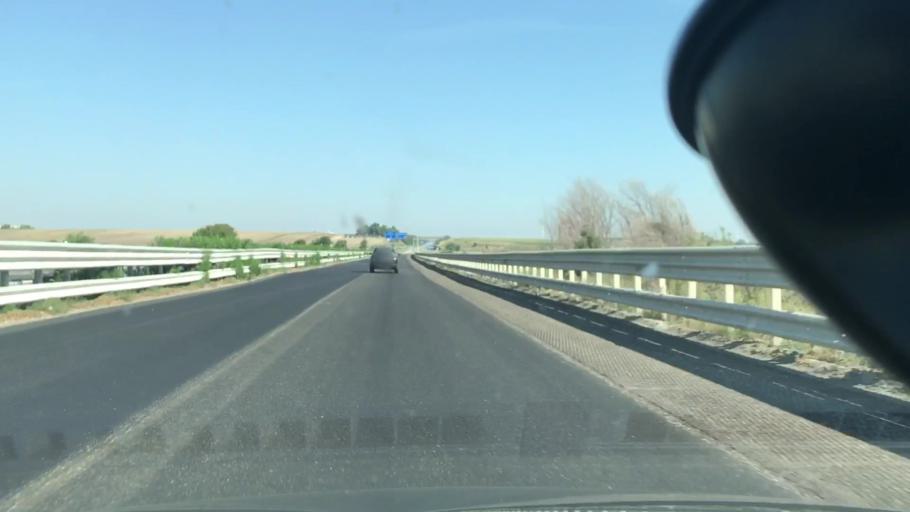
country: IT
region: Apulia
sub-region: Provincia di Foggia
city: Ordona
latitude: 41.3000
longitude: 15.5547
